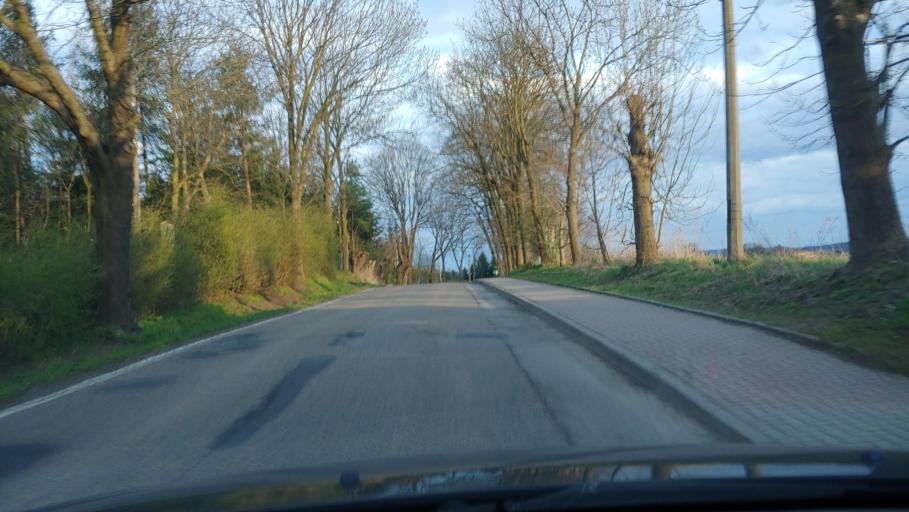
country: PL
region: Lesser Poland Voivodeship
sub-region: Powiat krakowski
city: Bolechowice
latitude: 50.1448
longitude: 19.7946
